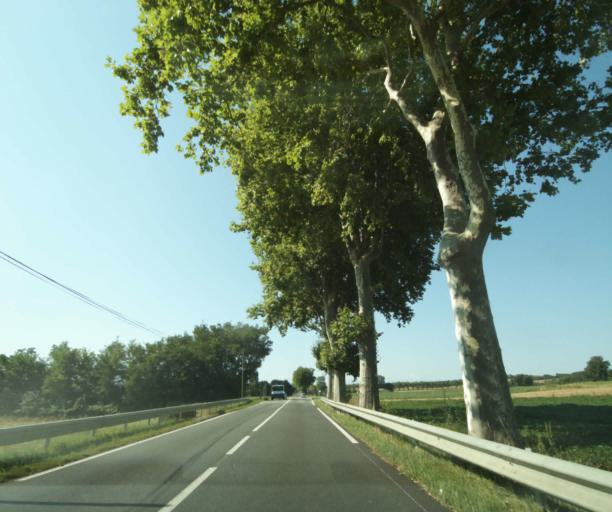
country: FR
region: Midi-Pyrenees
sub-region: Departement de la Haute-Garonne
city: Saint-Sulpice-sur-Leze
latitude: 43.3519
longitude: 1.3257
